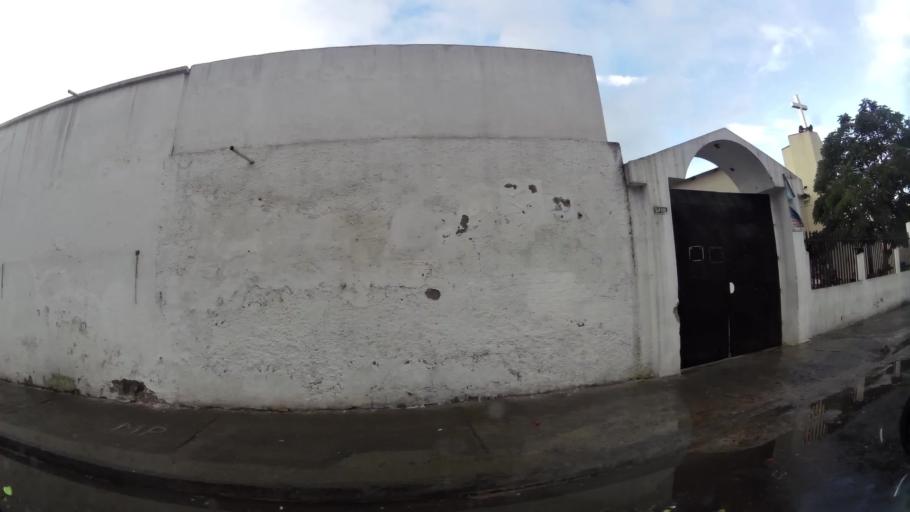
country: EC
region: Pichincha
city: Quito
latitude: -0.1065
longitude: -78.4935
